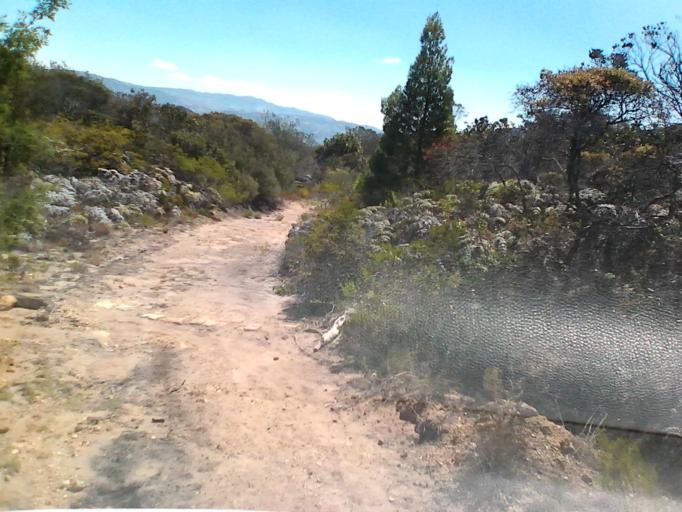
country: CO
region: Boyaca
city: Sachica
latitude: 5.5298
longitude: -73.5410
